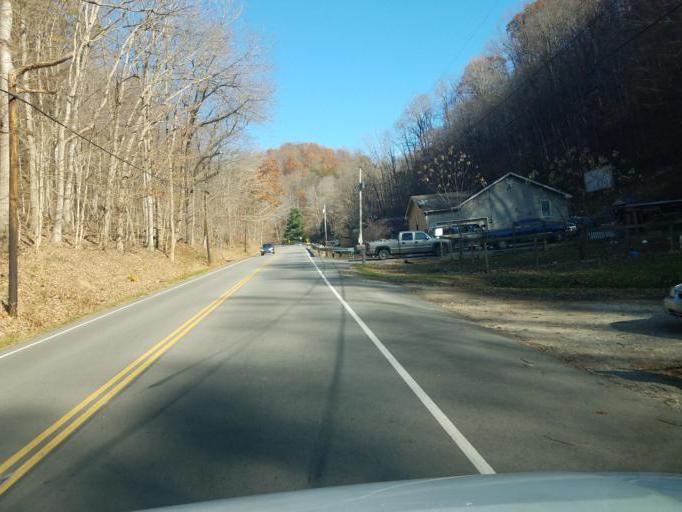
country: US
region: Ohio
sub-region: Scioto County
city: Rosemount
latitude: 38.7987
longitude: -82.9515
